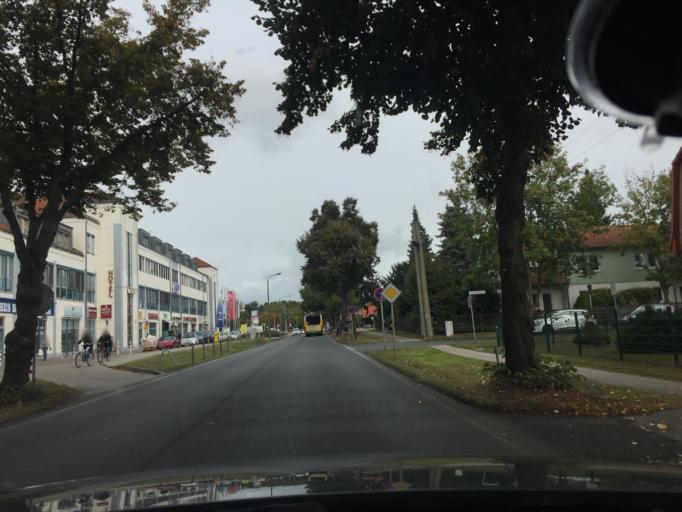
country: DE
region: Berlin
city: Hellersdorf
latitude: 52.5362
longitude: 13.6331
